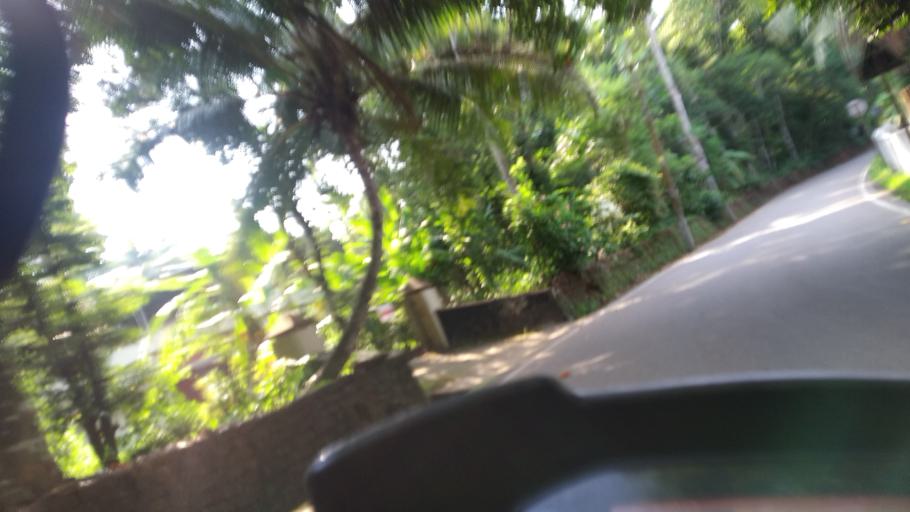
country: IN
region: Kerala
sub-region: Ernakulam
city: Piravam
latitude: 9.8558
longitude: 76.5246
